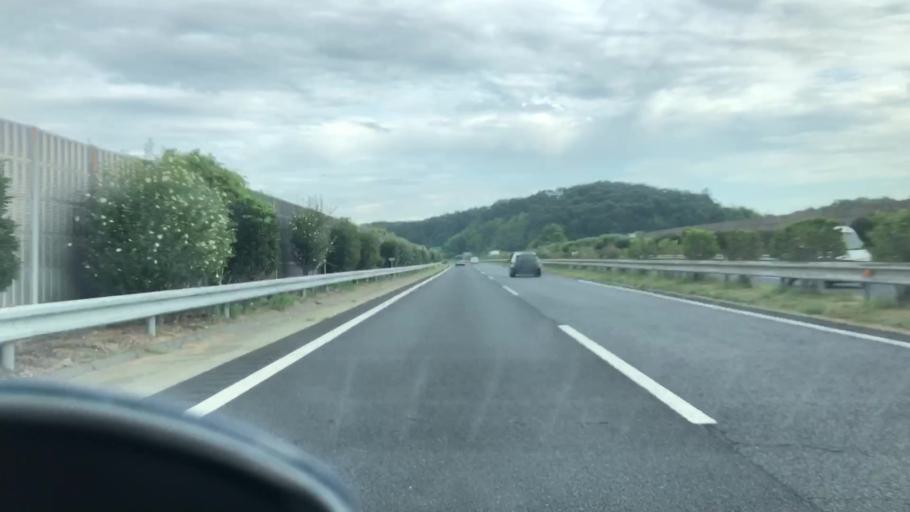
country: JP
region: Hyogo
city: Yashiro
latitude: 34.9037
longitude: 135.0666
